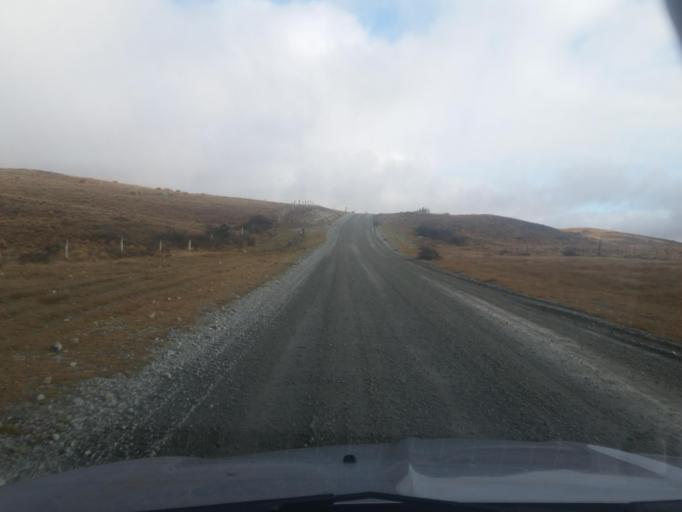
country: NZ
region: Canterbury
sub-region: Ashburton District
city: Methven
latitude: -43.6103
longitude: 171.0430
